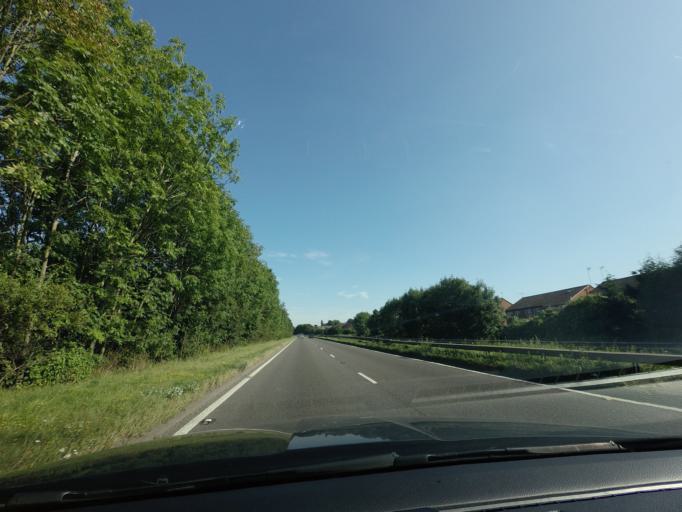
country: GB
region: England
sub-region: Derbyshire
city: Chesterfield
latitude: 53.2281
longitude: -1.4153
